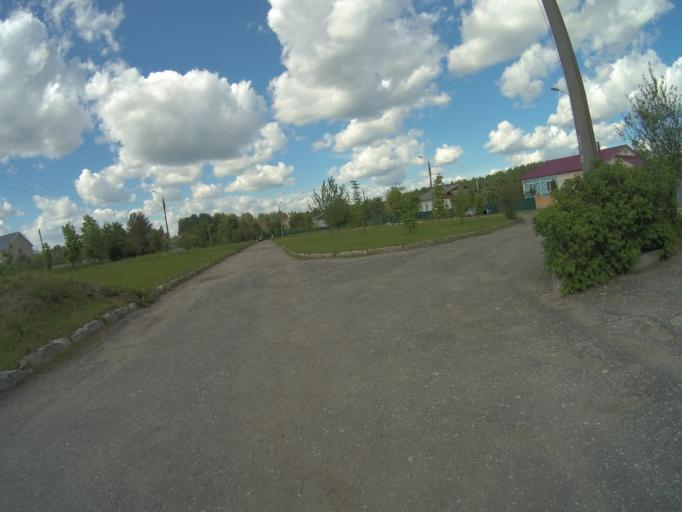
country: RU
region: Vladimir
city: Kommunar
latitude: 56.0591
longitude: 40.4941
